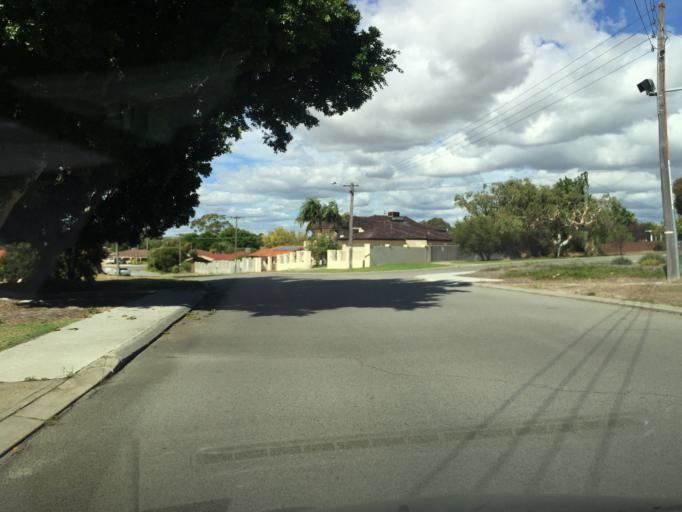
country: AU
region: Western Australia
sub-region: Canning
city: Willetton
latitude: -32.0584
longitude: 115.8922
